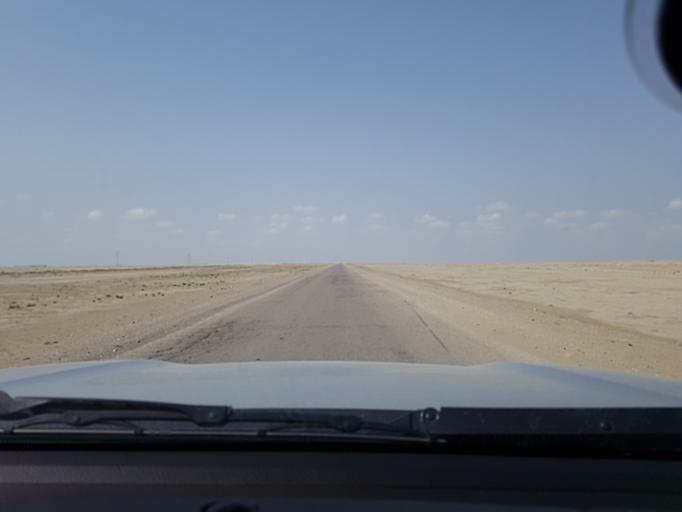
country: TM
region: Balkan
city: Gumdag
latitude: 38.6549
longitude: 54.3896
